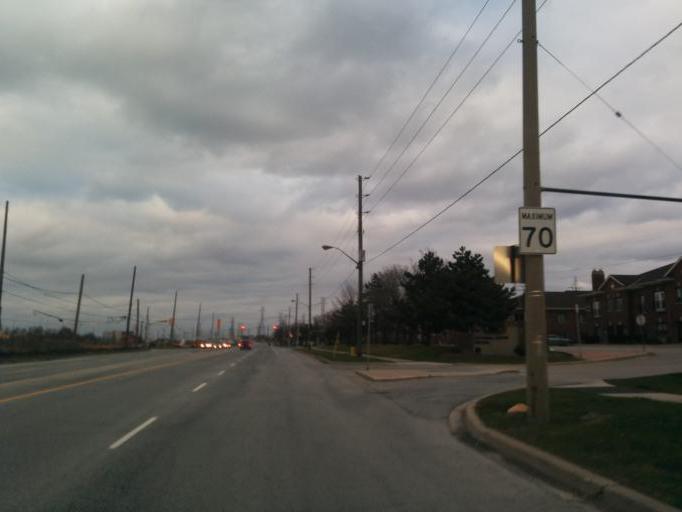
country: CA
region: Ontario
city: Etobicoke
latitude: 43.6615
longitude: -79.5921
